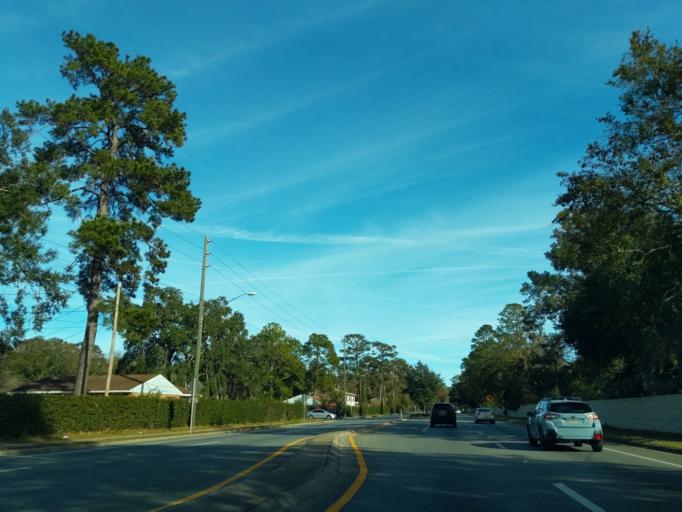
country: US
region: Florida
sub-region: Leon County
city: Tallahassee
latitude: 30.4126
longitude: -84.2698
